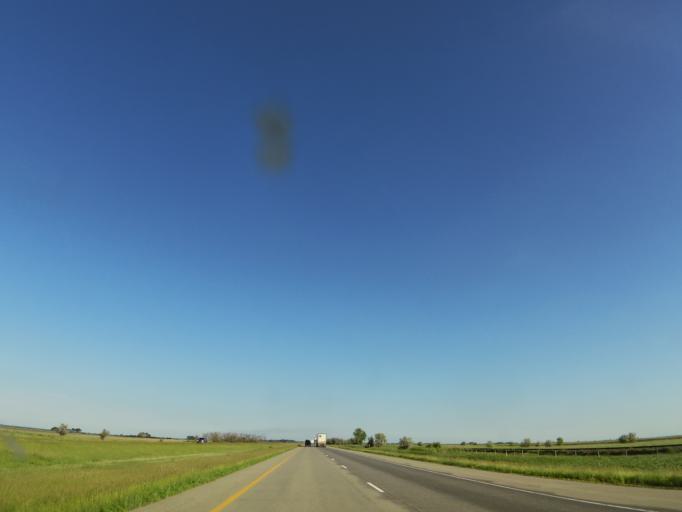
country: US
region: North Dakota
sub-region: Grand Forks County
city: Grand Forks
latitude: 48.0548
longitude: -97.1562
